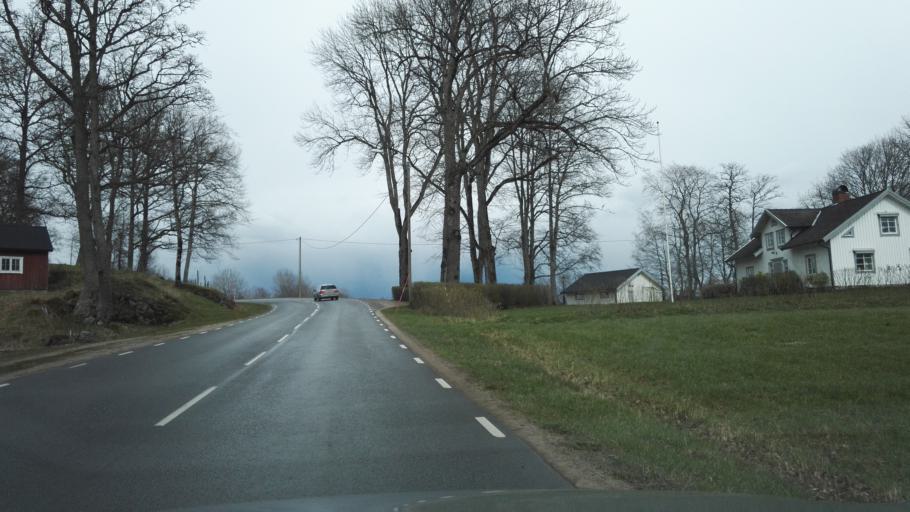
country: SE
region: Joenkoeping
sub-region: Vetlanda Kommun
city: Landsbro
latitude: 57.3094
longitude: 14.8682
